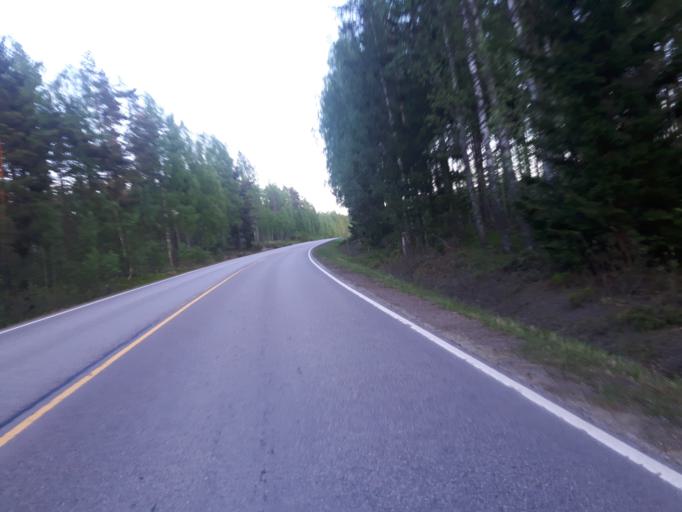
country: FI
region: Uusimaa
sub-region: Loviisa
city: Perna
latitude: 60.4596
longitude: 26.0687
